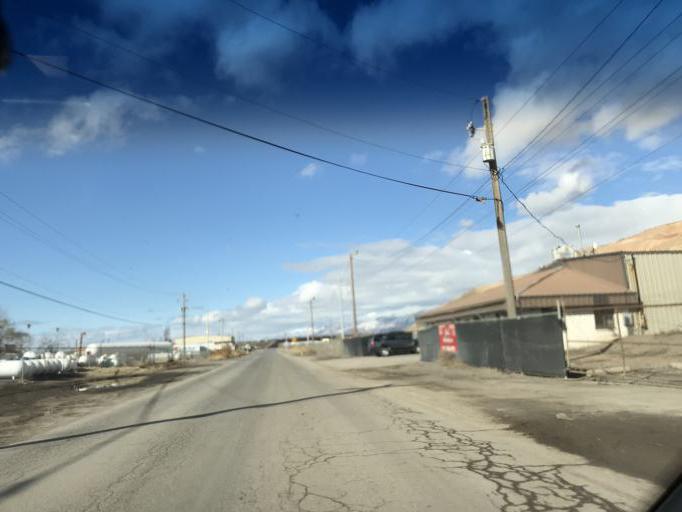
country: US
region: Utah
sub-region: Davis County
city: North Salt Lake
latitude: 40.8089
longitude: -111.9208
